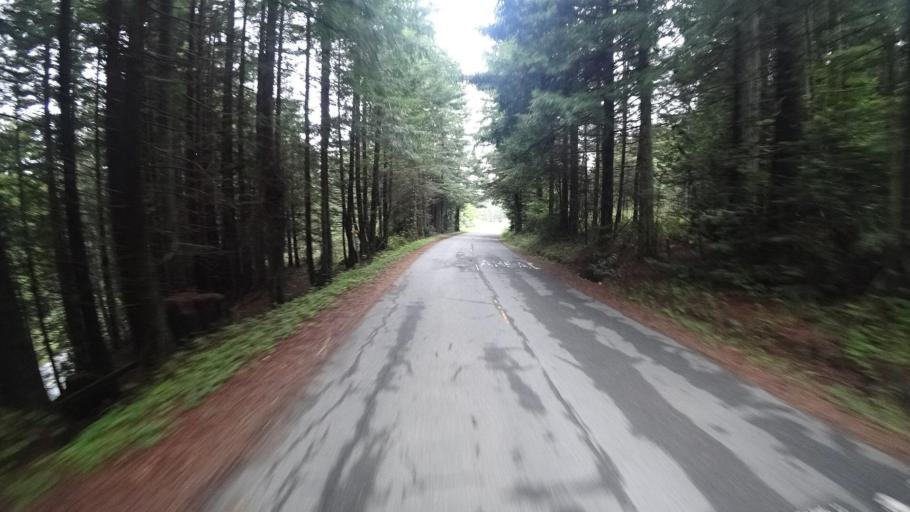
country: US
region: California
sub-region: Humboldt County
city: Blue Lake
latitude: 40.8754
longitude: -123.9784
